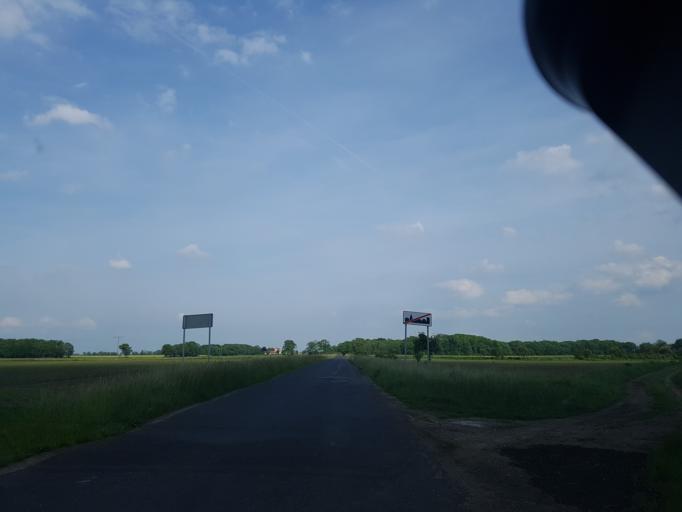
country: PL
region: Lower Silesian Voivodeship
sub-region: Powiat wroclawski
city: Zorawina
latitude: 50.9109
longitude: 17.0692
